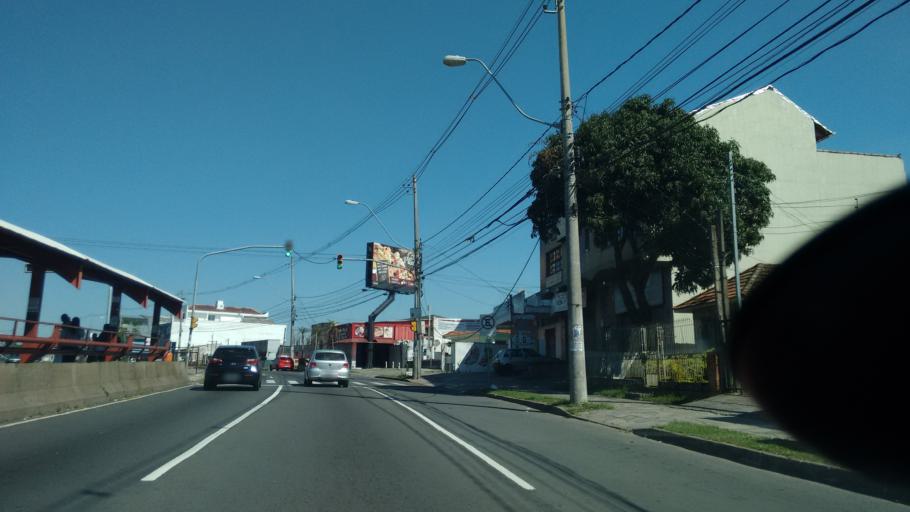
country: BR
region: Rio Grande do Sul
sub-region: Cachoeirinha
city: Cachoeirinha
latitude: -30.0136
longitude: -51.1234
